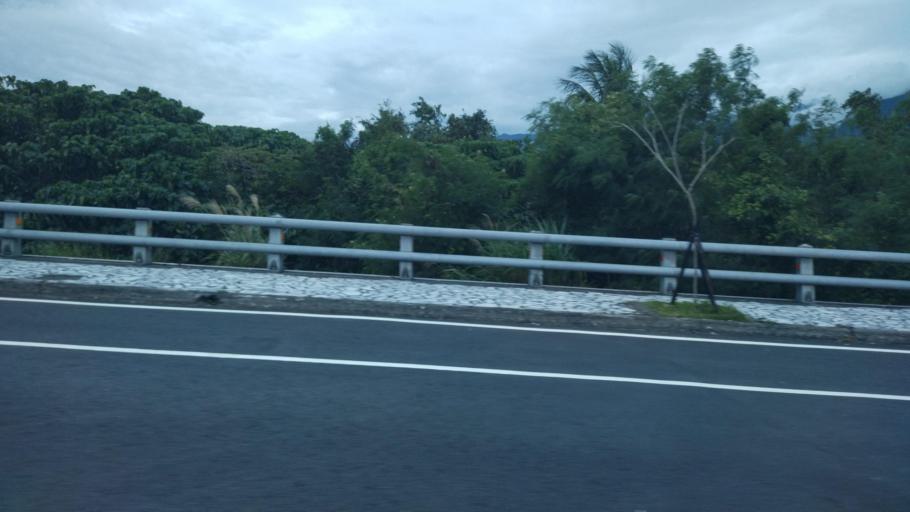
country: TW
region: Taiwan
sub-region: Hualien
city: Hualian
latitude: 24.0089
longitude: 121.6091
